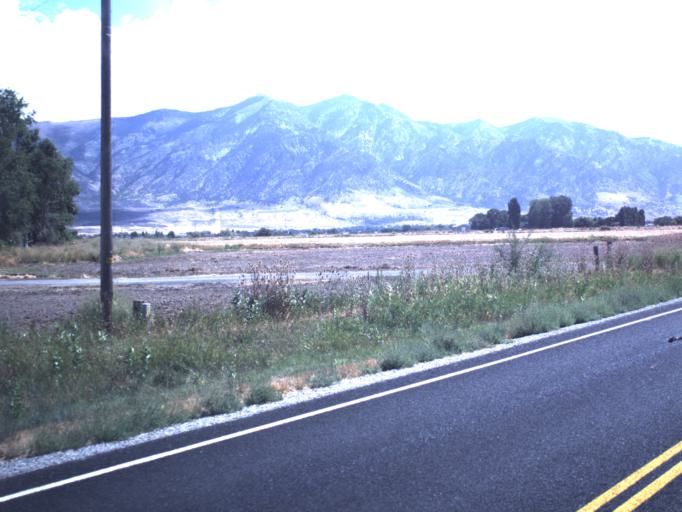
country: US
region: Utah
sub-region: Box Elder County
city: Elwood
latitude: 41.6474
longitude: -112.1349
